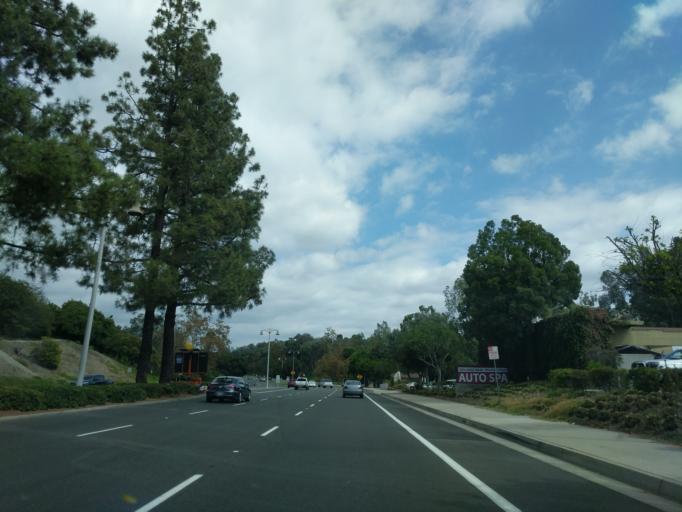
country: US
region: California
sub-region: Orange County
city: Lake Forest
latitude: 33.6269
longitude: -117.6763
